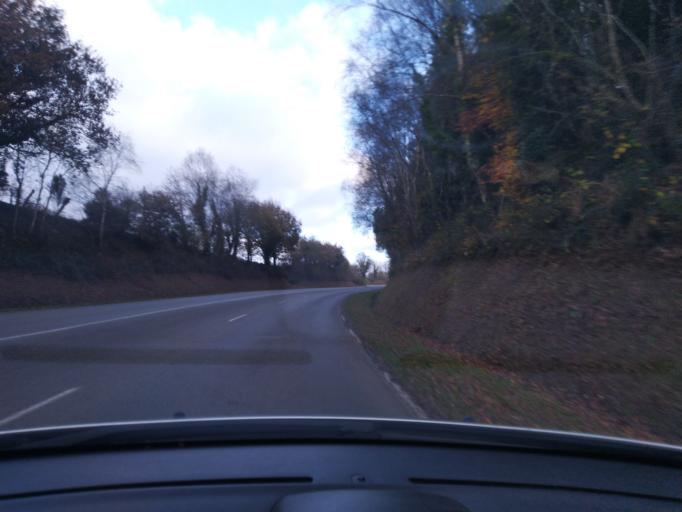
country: FR
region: Brittany
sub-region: Departement du Finistere
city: Guerlesquin
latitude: 48.5622
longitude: -3.6233
